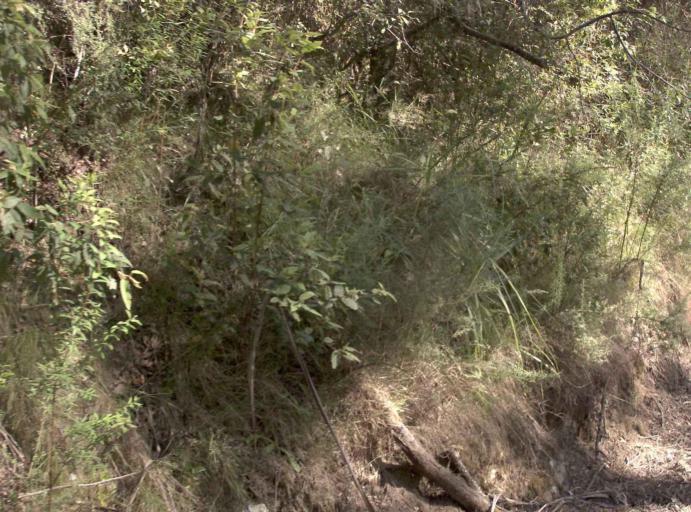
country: AU
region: Victoria
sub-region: East Gippsland
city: Lakes Entrance
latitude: -37.4919
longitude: 148.5557
